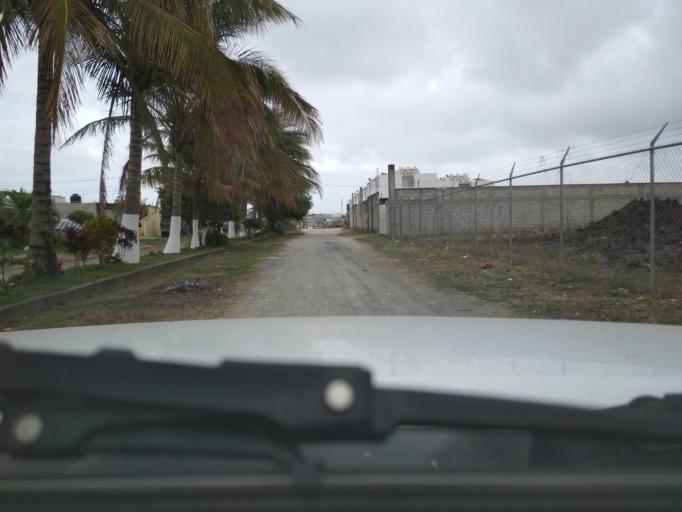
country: MX
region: Veracruz
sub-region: Veracruz
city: Fraccionamiento Geovillas los Pinos
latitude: 19.2075
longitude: -96.2275
